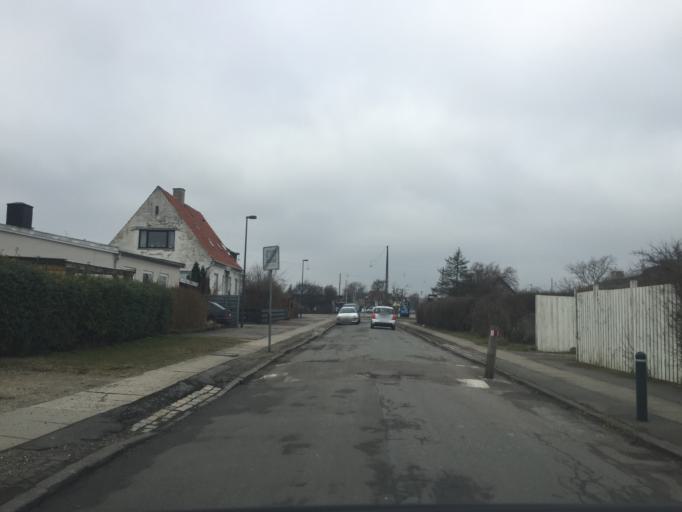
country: DK
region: Capital Region
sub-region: Tarnby Kommune
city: Tarnby
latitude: 55.6410
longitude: 12.5916
